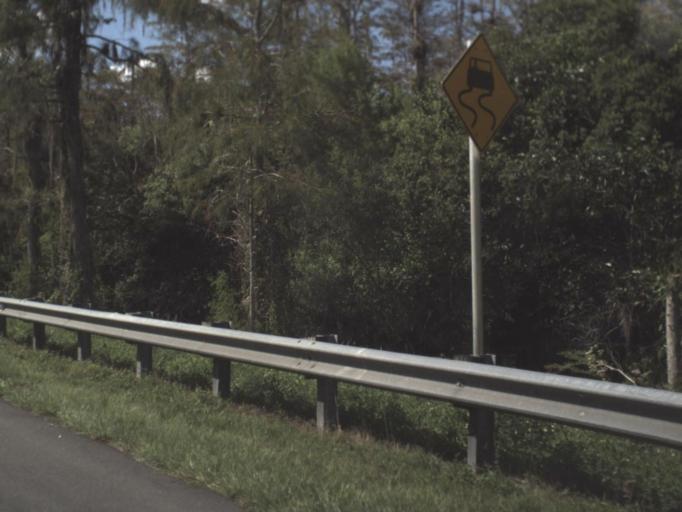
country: US
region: Florida
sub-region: Miami-Dade County
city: Kendall West
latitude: 25.8468
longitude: -80.9334
